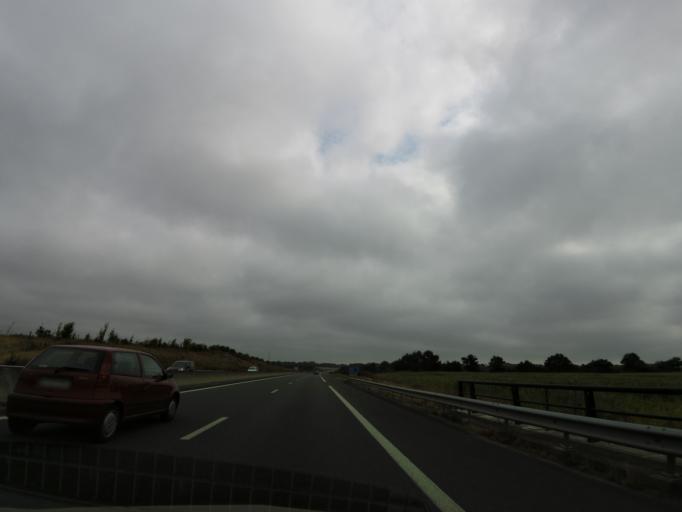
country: FR
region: Pays de la Loire
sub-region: Departement de la Vendee
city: La Roche-sur-Yon
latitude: 46.6466
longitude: -1.3915
